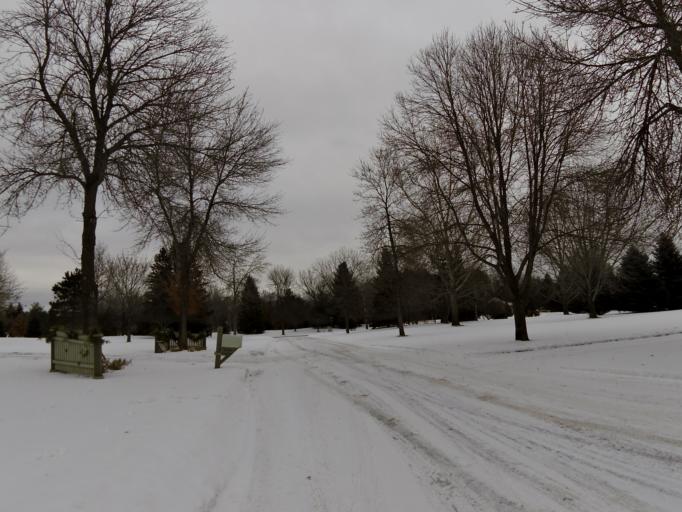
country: US
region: Minnesota
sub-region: Washington County
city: Lake Elmo
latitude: 44.9575
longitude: -92.8516
